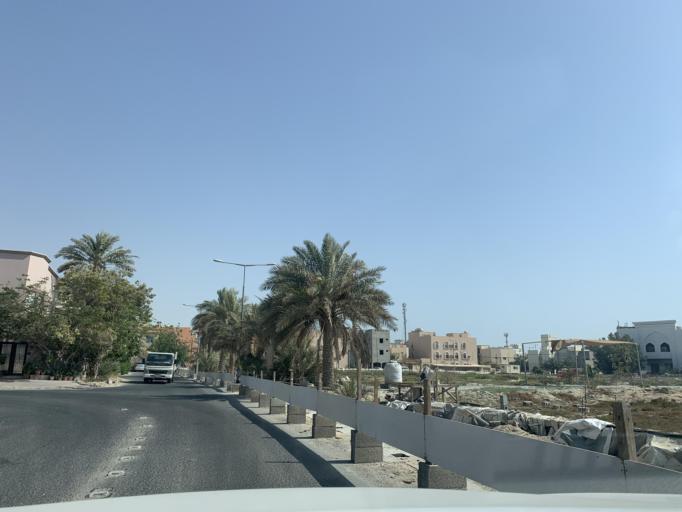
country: BH
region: Manama
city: Jidd Hafs
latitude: 26.2250
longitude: 50.4652
